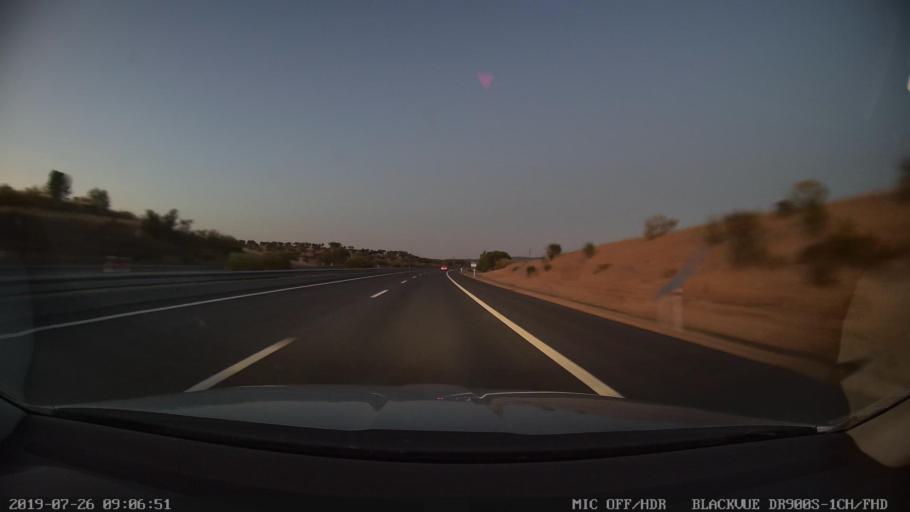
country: PT
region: Evora
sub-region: Estremoz
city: Estremoz
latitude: 38.7413
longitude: -7.7491
